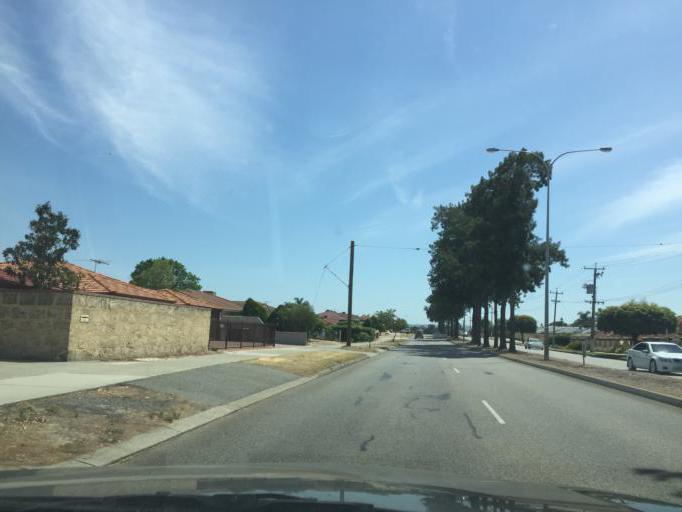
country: AU
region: Western Australia
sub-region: Gosnells
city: Thornlie
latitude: -32.0737
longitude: 115.9631
